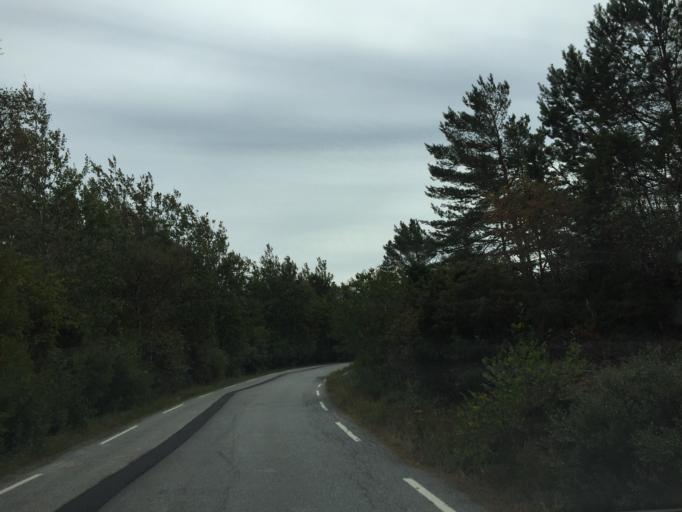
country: NO
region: Ostfold
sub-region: Hvaler
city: Skjaerhalden
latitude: 59.0478
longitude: 10.9532
